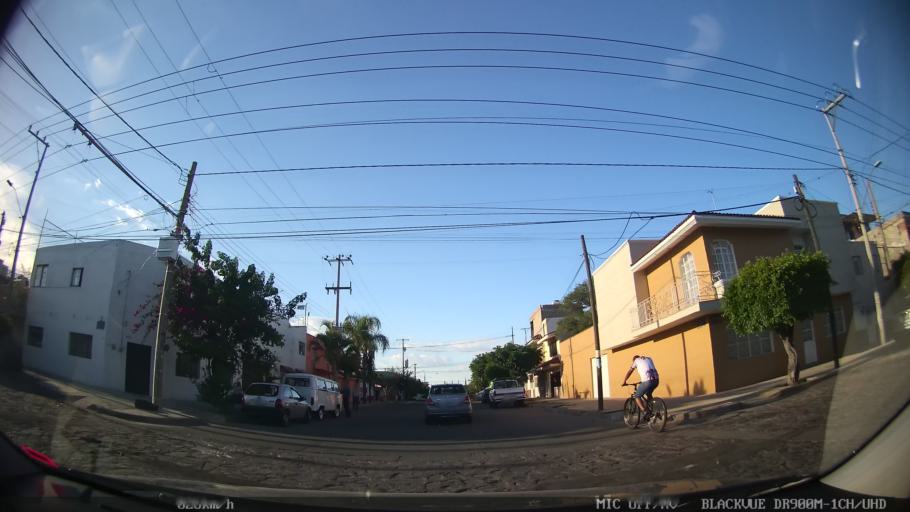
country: MX
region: Jalisco
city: Tlaquepaque
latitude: 20.6988
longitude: -103.3028
